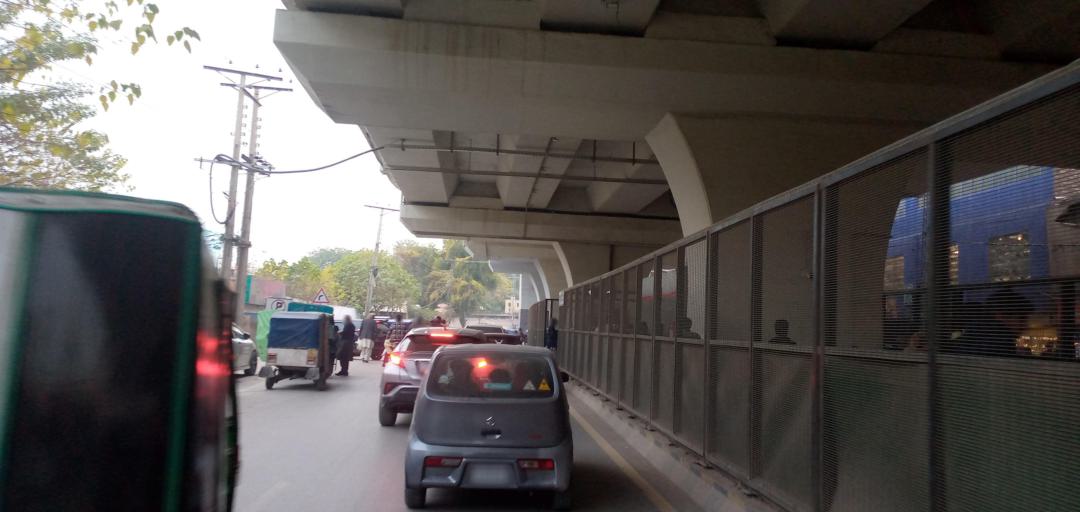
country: PK
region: Khyber Pakhtunkhwa
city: Peshawar
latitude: 33.9948
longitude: 71.5382
